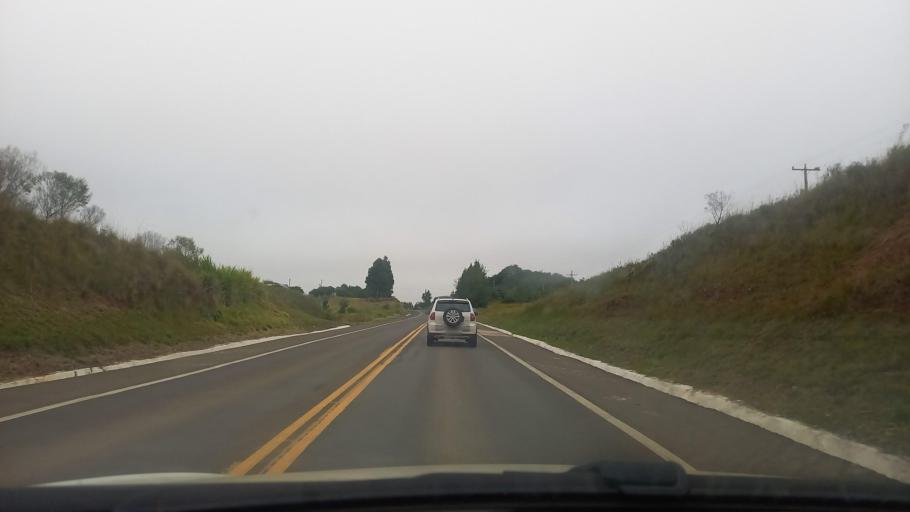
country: BR
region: Rio Grande do Sul
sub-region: Rosario Do Sul
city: Rosario do Sul
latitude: -30.2678
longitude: -54.9738
